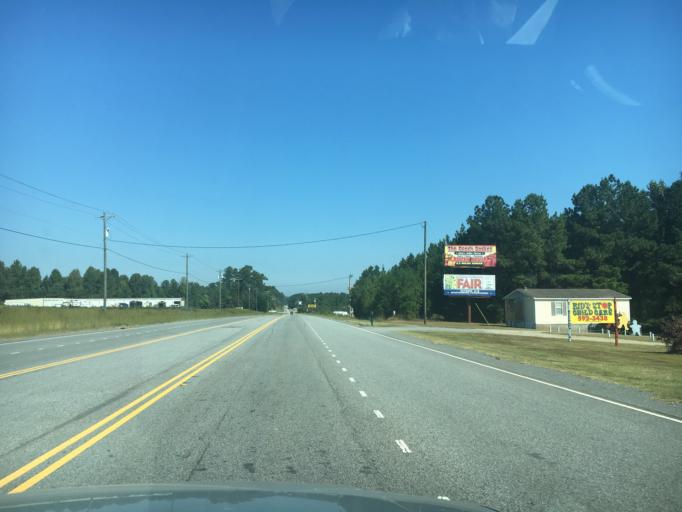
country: US
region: South Carolina
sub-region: Spartanburg County
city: Inman
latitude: 35.0955
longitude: -82.0401
